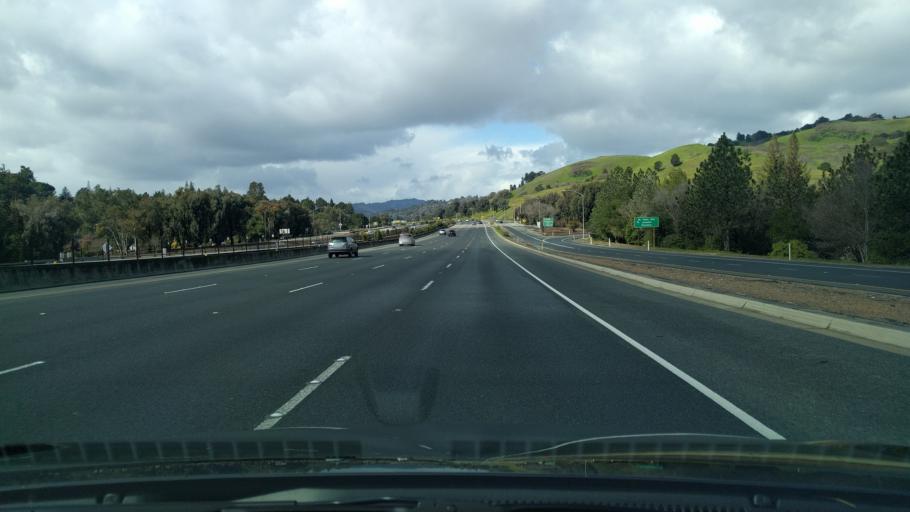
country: US
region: California
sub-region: Contra Costa County
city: Saranap
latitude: 37.8982
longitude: -122.0918
